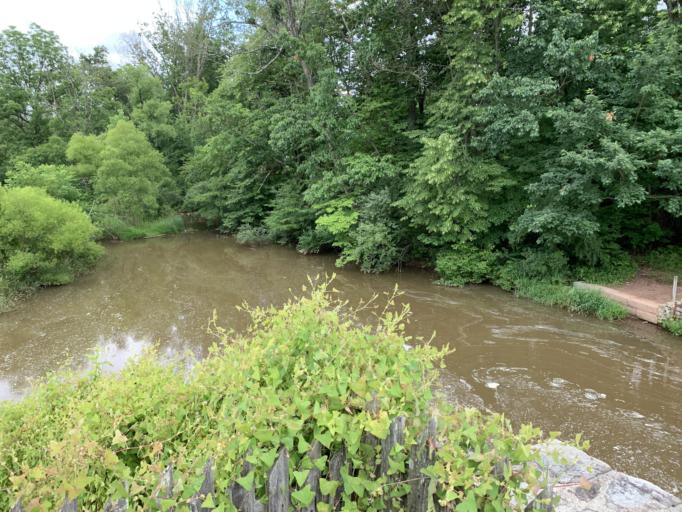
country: US
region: Pennsylvania
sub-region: Berks County
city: Birdsboro
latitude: 40.2948
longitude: -75.7950
